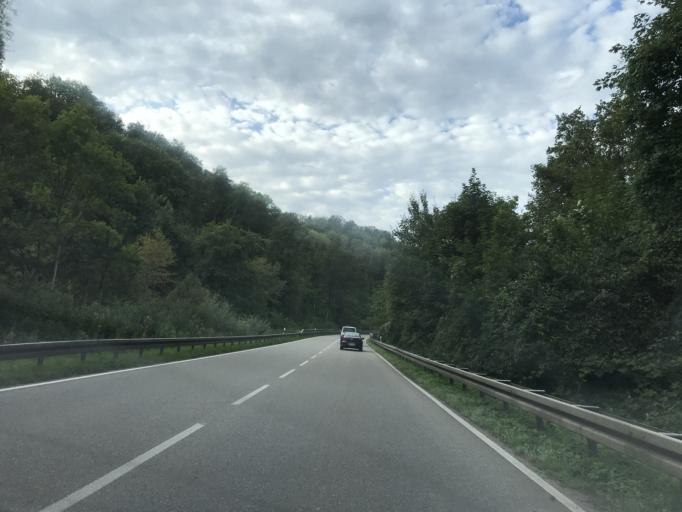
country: DE
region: Baden-Wuerttemberg
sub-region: Freiburg Region
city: Schworstadt
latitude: 47.5881
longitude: 7.9101
